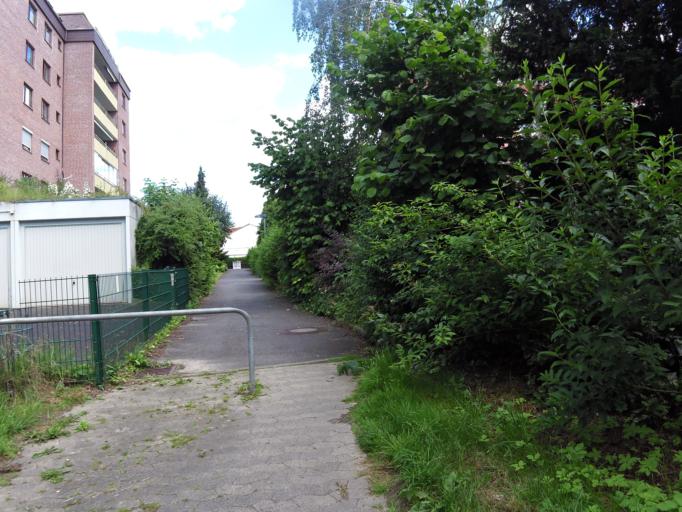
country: DE
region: Lower Saxony
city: Goettingen
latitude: 51.5100
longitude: 9.9484
